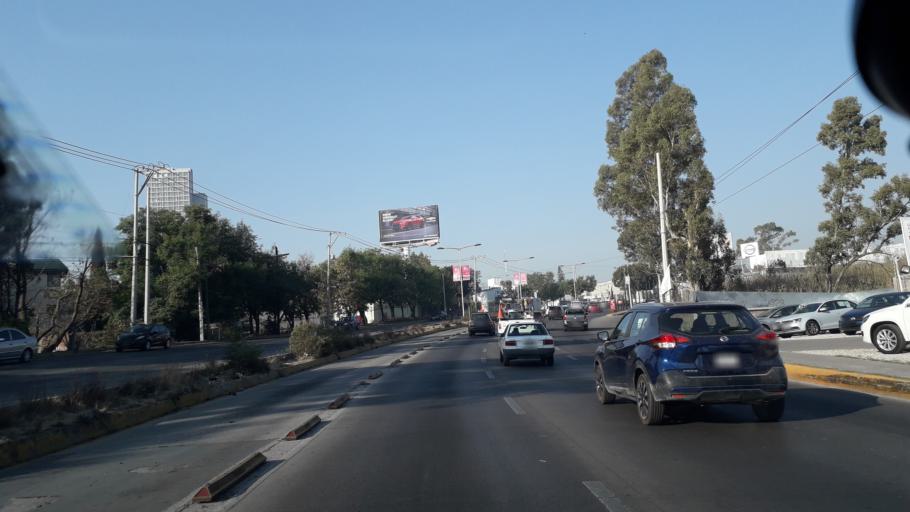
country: MX
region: Puebla
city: Puebla
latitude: 19.0410
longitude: -98.2385
